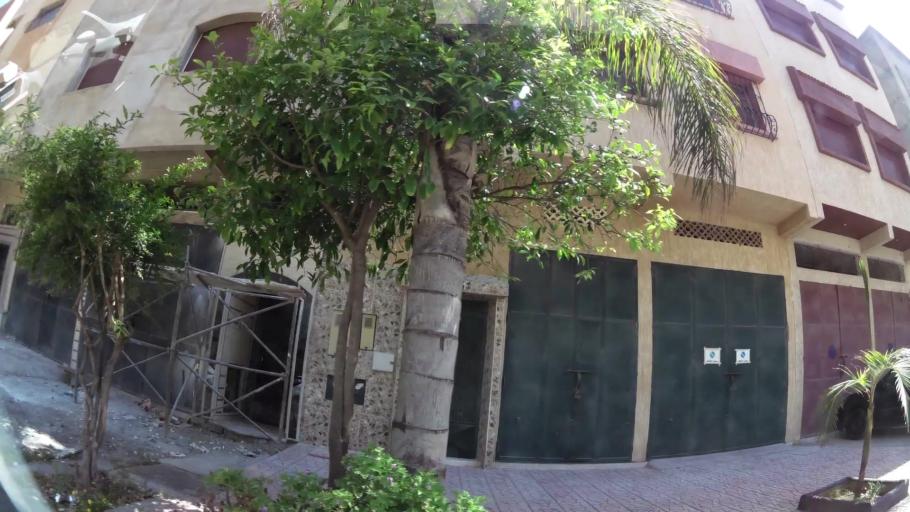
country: MA
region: Rabat-Sale-Zemmour-Zaer
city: Sale
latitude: 34.0752
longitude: -6.7882
